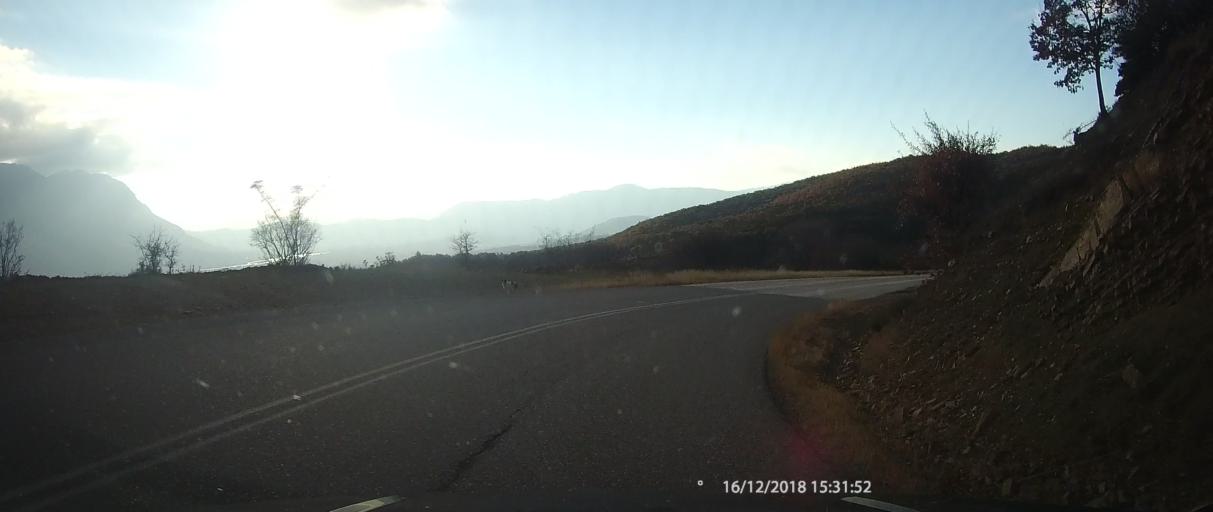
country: GR
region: Epirus
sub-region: Nomos Ioanninon
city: Konitsa
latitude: 40.0706
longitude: 20.7434
